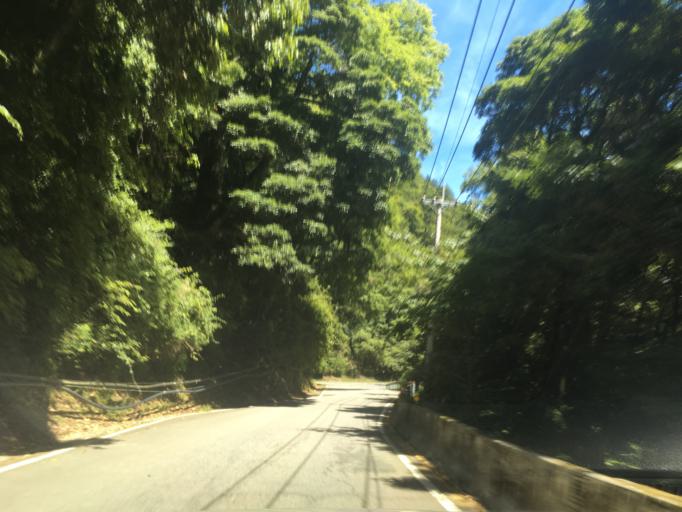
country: TW
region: Taiwan
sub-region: Nantou
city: Puli
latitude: 24.2167
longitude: 121.2652
